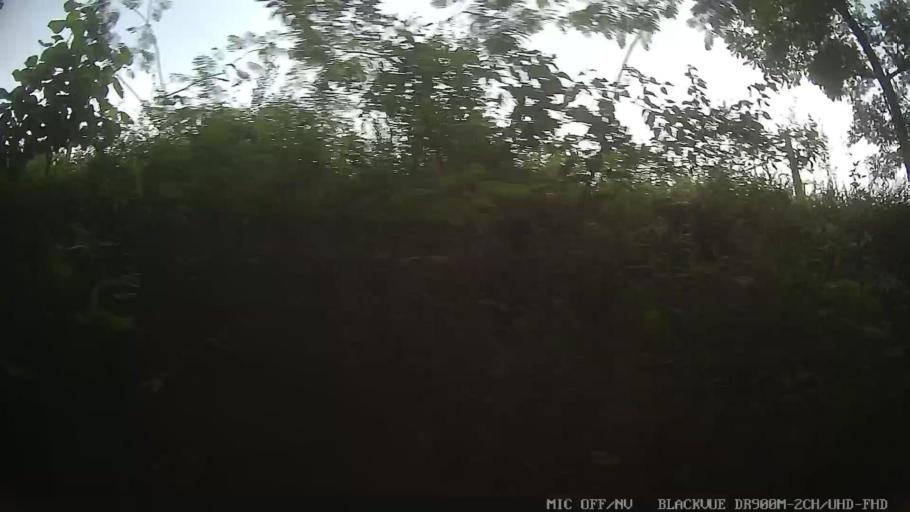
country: BR
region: Sao Paulo
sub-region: Atibaia
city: Atibaia
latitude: -23.1753
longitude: -46.5869
